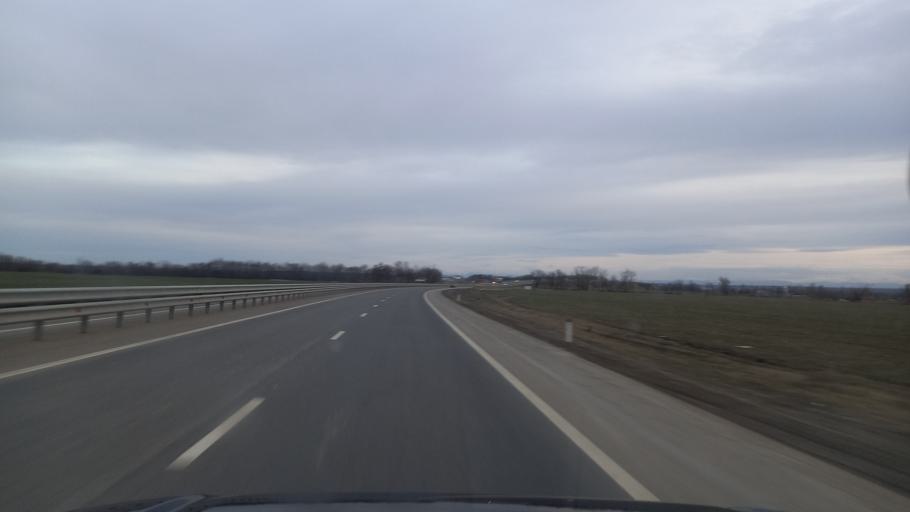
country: RU
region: Adygeya
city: Khanskaya
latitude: 44.7077
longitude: 39.9654
